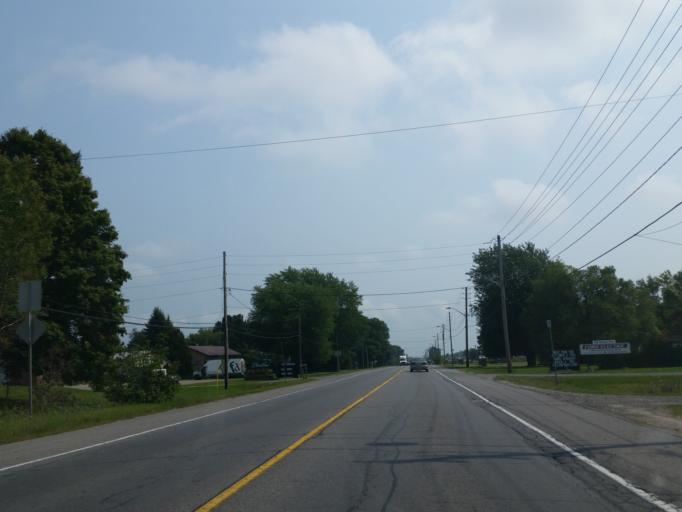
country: CA
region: Ontario
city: Brockville
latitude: 44.6085
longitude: -75.7281
